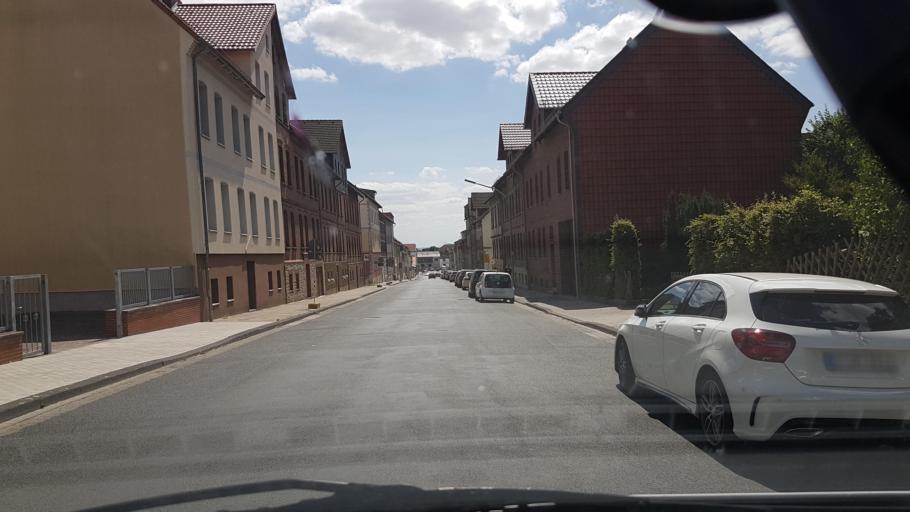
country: DE
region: Lower Saxony
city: Schoningen
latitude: 52.1426
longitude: 10.9748
